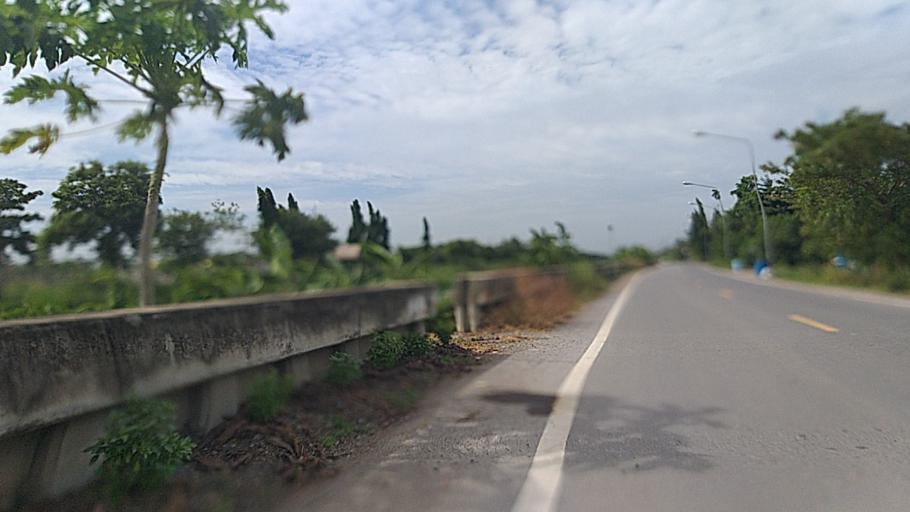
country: TH
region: Pathum Thani
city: Nong Suea
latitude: 14.0498
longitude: 100.8928
